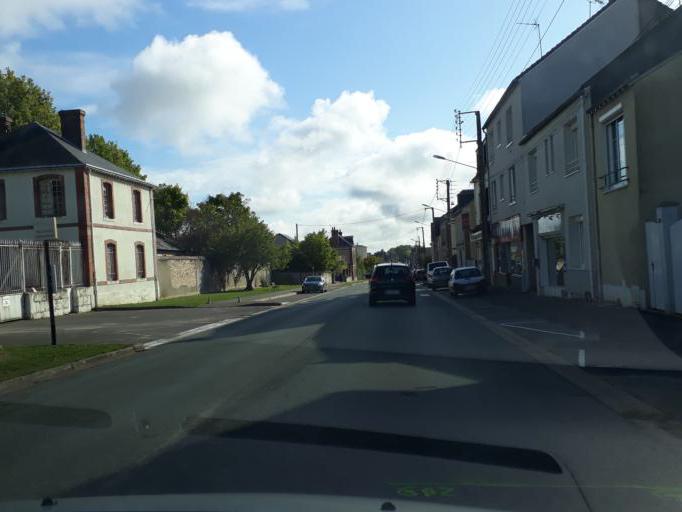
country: FR
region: Centre
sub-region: Departement d'Eure-et-Loir
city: Chateaudun
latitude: 48.0716
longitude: 1.3408
